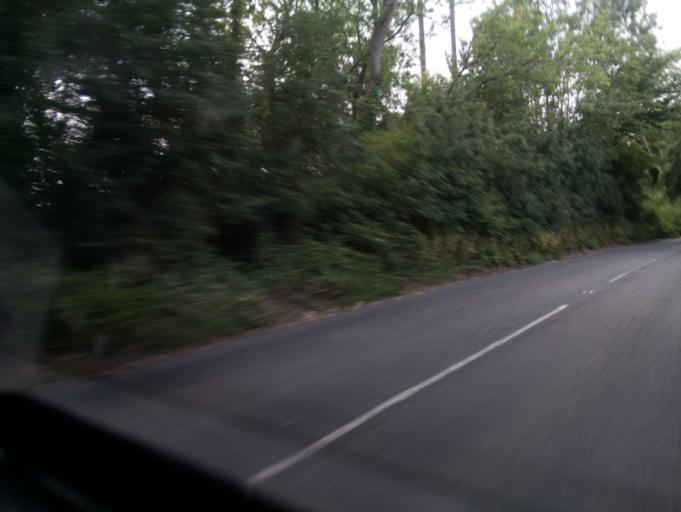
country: GB
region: England
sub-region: Gloucestershire
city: Chipping Campden
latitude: 52.0047
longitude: -1.7609
